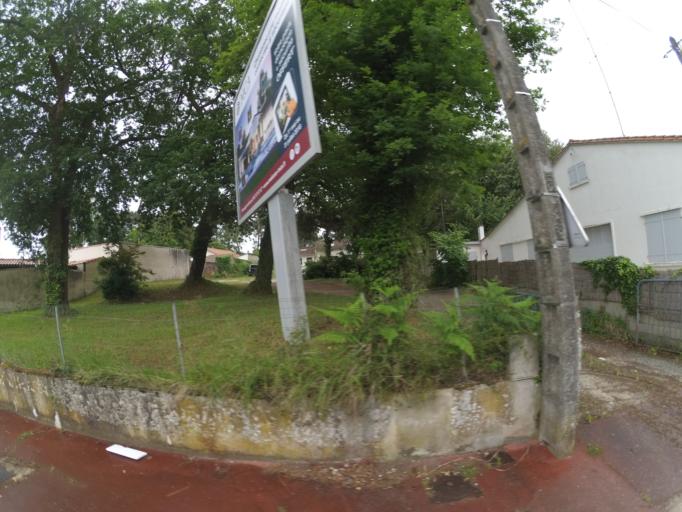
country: FR
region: Poitou-Charentes
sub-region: Departement de la Charente-Maritime
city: Saint-Georges-de-Didonne
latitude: 45.6174
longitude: -1.0038
